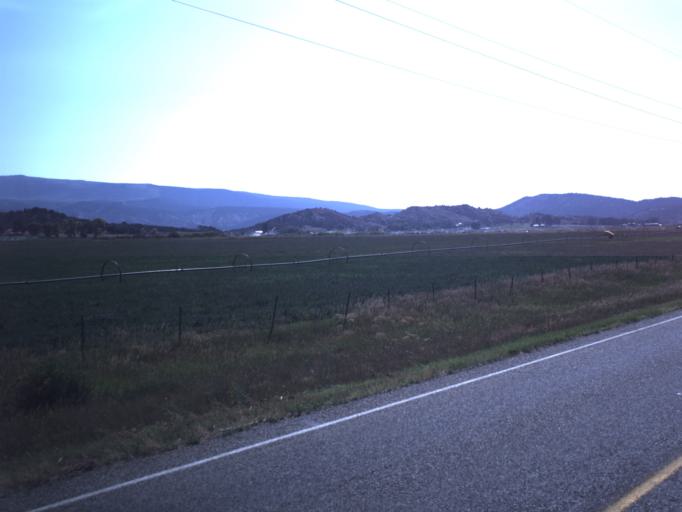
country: US
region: Utah
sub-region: Duchesne County
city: Duchesne
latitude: 40.3797
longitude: -110.7367
